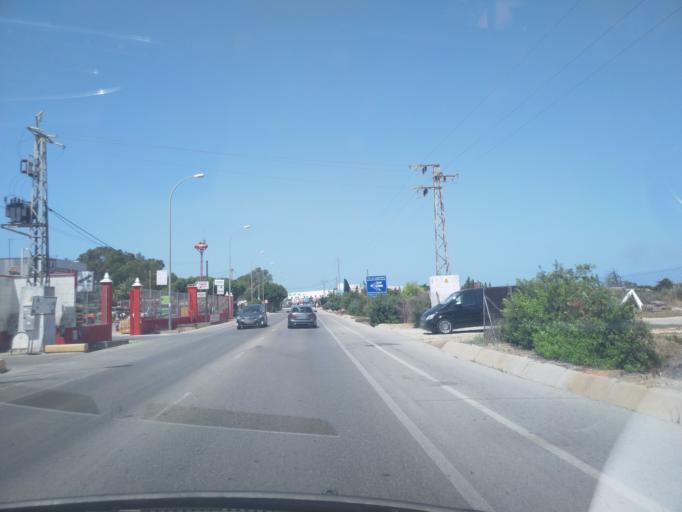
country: ES
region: Andalusia
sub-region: Provincia de Cadiz
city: Chiclana de la Frontera
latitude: 36.3958
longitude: -6.1622
